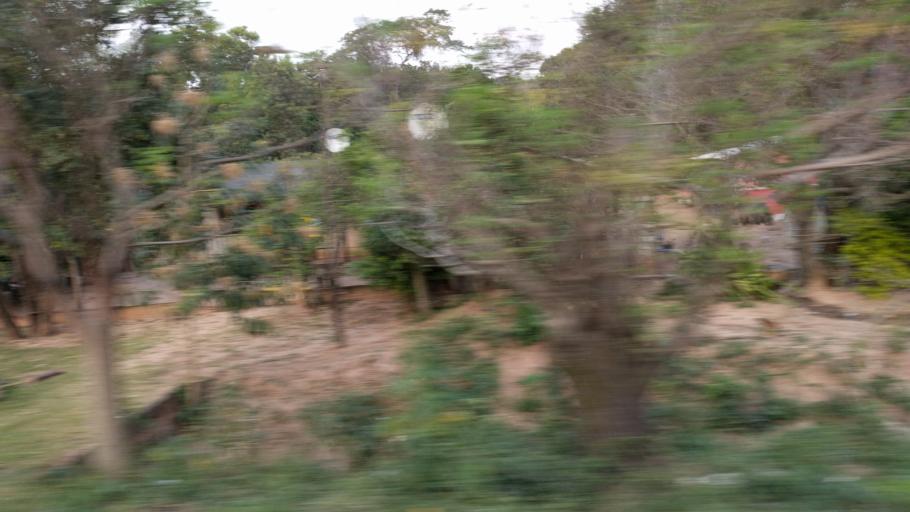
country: BO
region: Santa Cruz
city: Santa Rita
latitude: -17.9706
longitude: -63.3639
